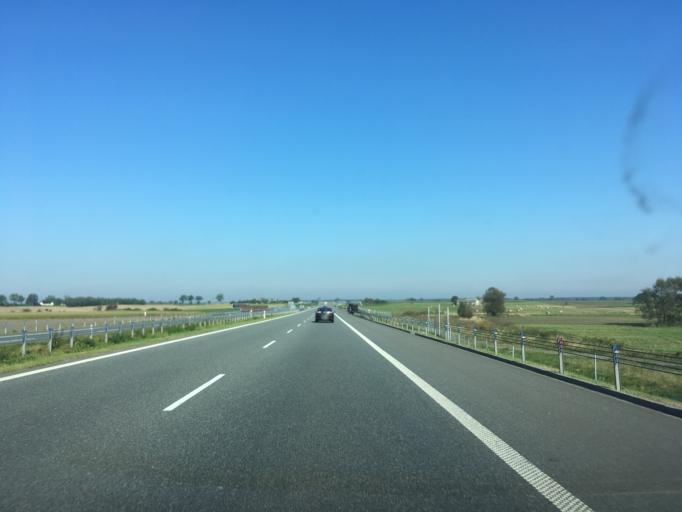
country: PL
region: Kujawsko-Pomorskie
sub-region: Powiat torunski
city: Lubicz Dolny
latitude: 53.1137
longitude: 18.7447
